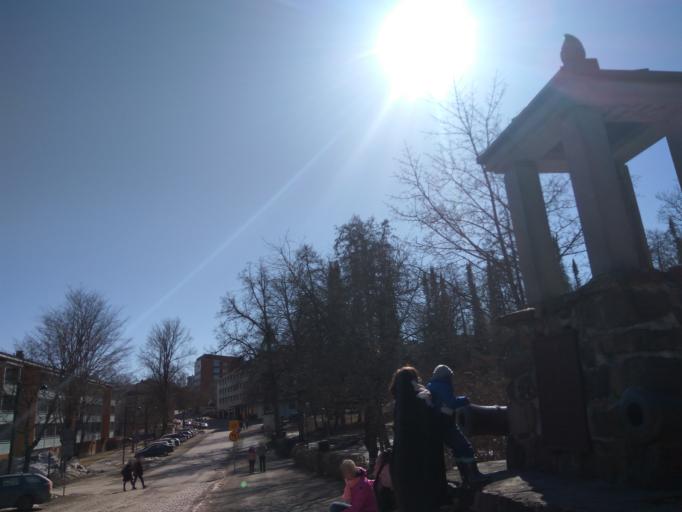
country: FI
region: South Karelia
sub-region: Lappeenranta
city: Lappeenranta
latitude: 61.0629
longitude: 28.1840
